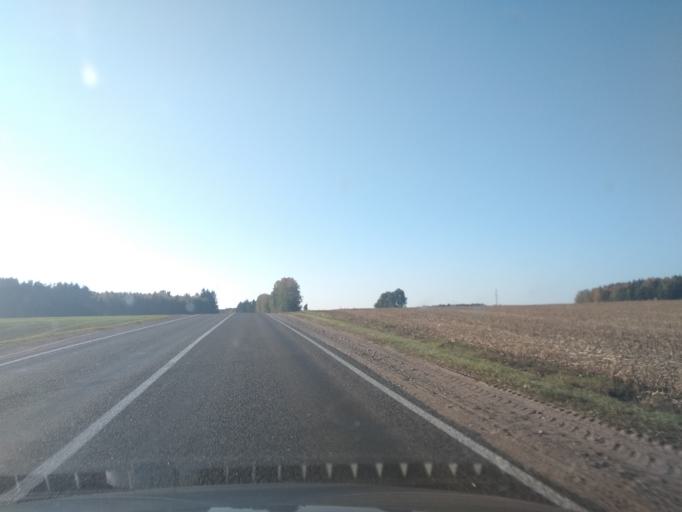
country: BY
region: Grodnenskaya
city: Vyalikaya Byerastavitsa
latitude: 53.1179
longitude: 24.0521
